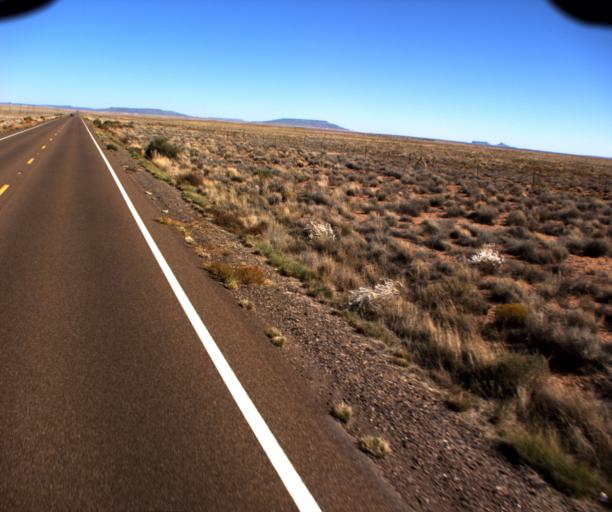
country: US
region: Arizona
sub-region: Navajo County
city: Winslow
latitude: 35.1142
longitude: -110.5171
